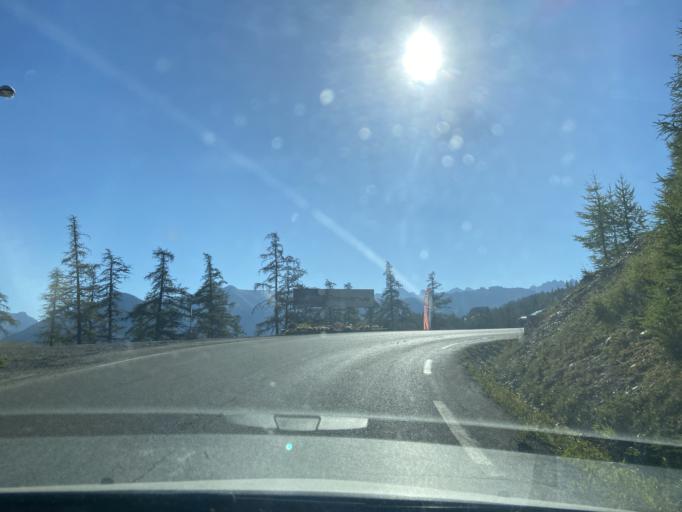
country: FR
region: Provence-Alpes-Cote d'Azur
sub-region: Departement des Hautes-Alpes
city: Guillestre
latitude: 44.6254
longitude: 6.6297
